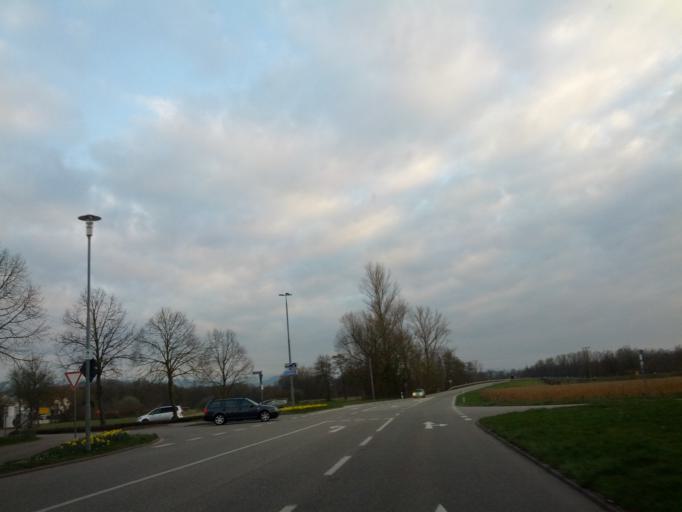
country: DE
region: Baden-Wuerttemberg
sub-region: Freiburg Region
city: Umkirch
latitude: 48.0474
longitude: 7.7802
